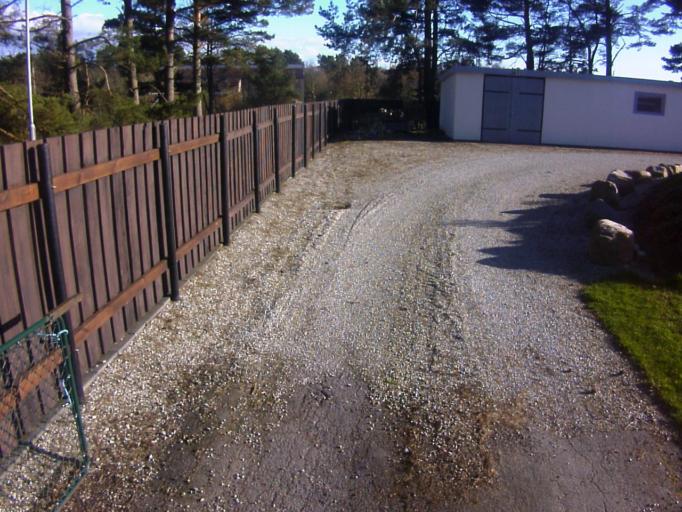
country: SE
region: Skane
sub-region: Kavlinge Kommun
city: Hofterup
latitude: 55.8092
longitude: 12.9760
